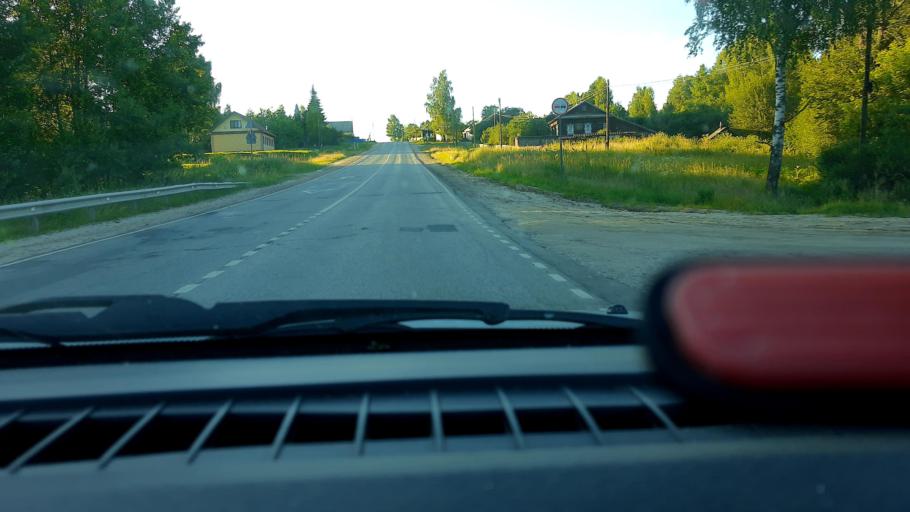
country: RU
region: Nizjnij Novgorod
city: Krasnyye Baki
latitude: 57.0633
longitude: 45.1376
